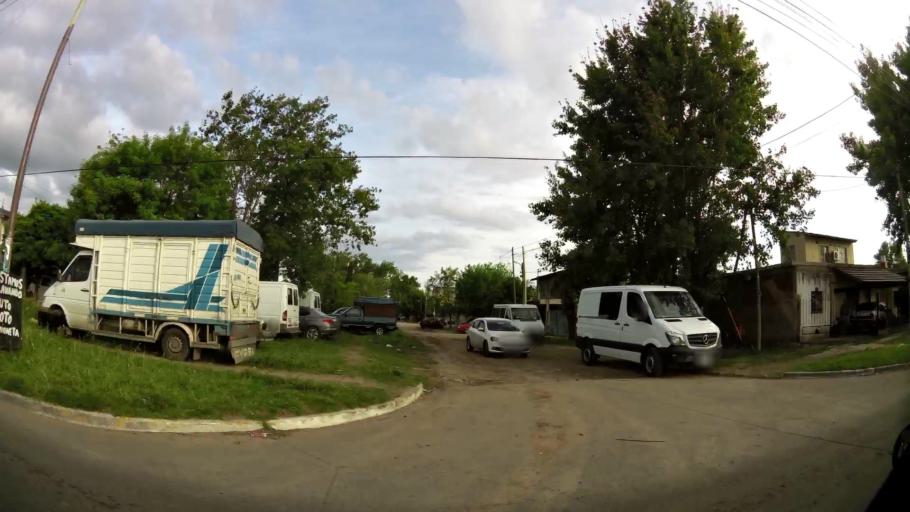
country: AR
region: Buenos Aires
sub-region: Partido de Quilmes
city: Quilmes
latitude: -34.7461
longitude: -58.2502
